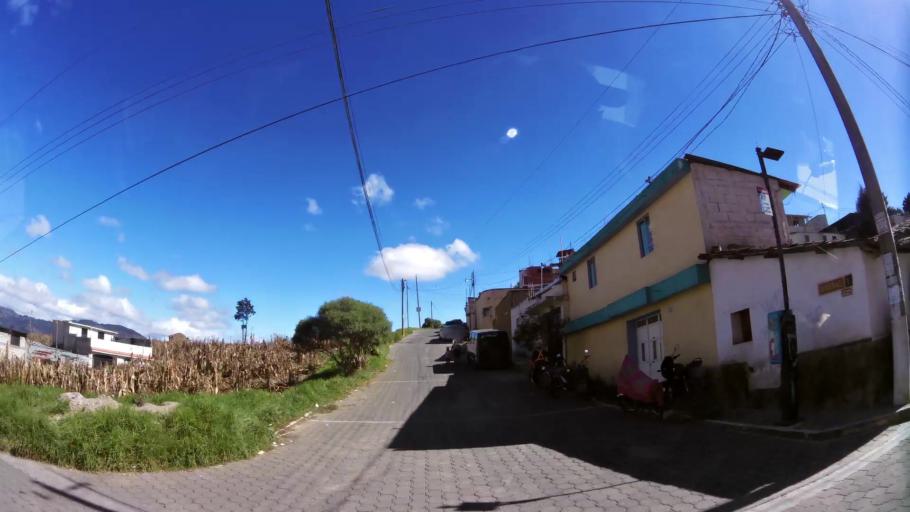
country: GT
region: Quetzaltenango
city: Quetzaltenango
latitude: 14.8369
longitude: -91.5016
